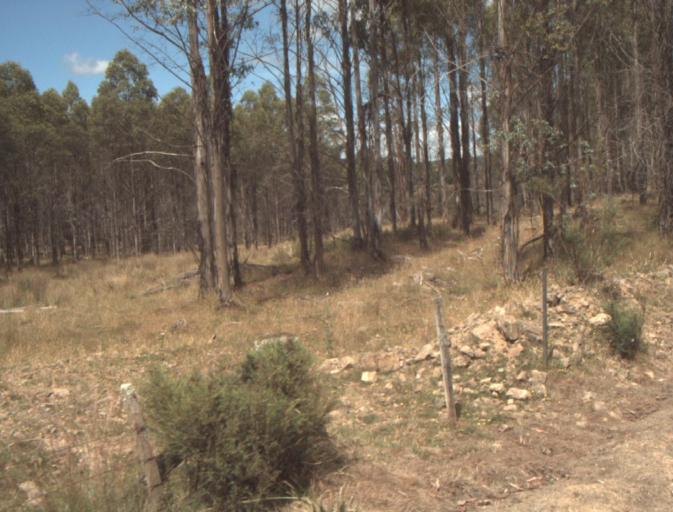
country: AU
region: Tasmania
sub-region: Dorset
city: Scottsdale
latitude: -41.4103
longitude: 147.5283
